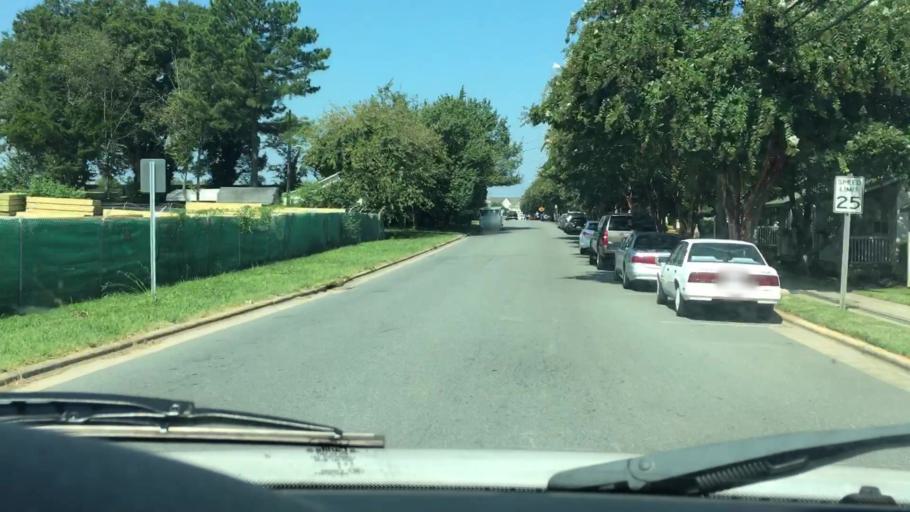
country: US
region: North Carolina
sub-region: Mecklenburg County
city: Cornelius
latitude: 35.4985
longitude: -80.8576
